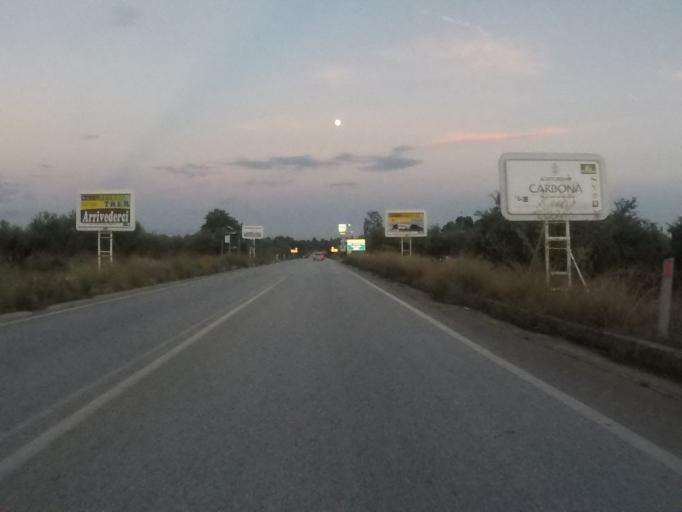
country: IT
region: Sicily
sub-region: Trapani
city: Castelvetrano
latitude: 37.6579
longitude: 12.8160
